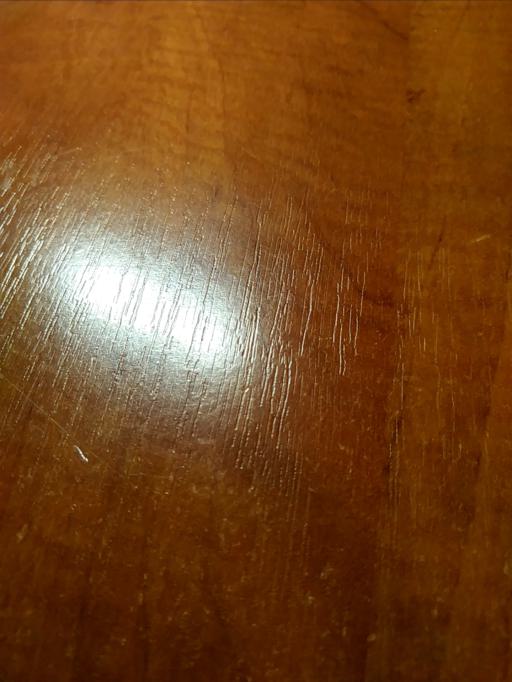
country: RU
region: Tverskaya
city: Staraya Toropa
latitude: 56.3473
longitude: 31.8275
